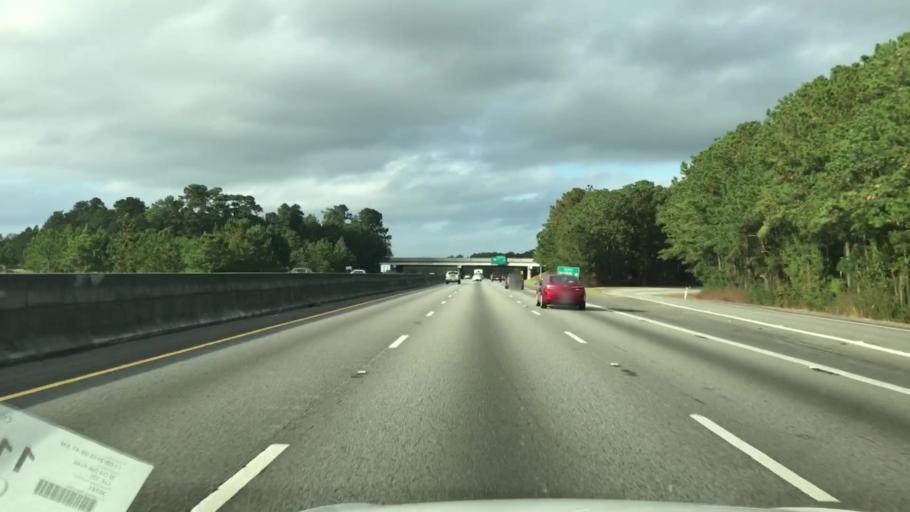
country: US
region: South Carolina
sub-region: Berkeley County
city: Ladson
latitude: 32.9760
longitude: -80.0765
